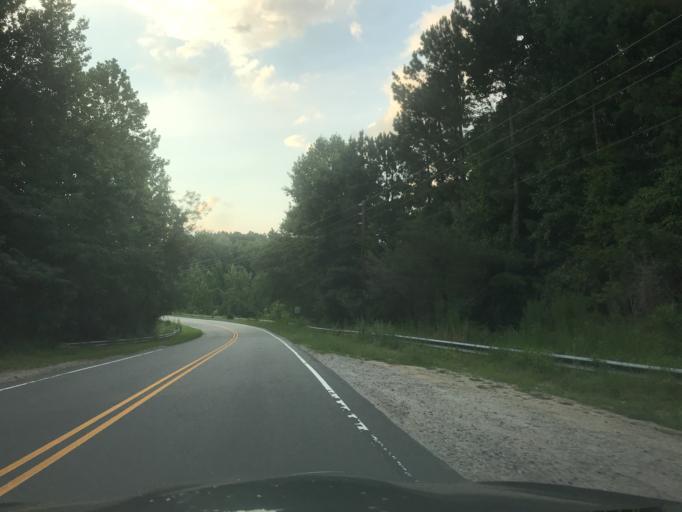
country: US
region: North Carolina
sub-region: Wake County
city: Wake Forest
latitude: 35.9283
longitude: -78.6058
